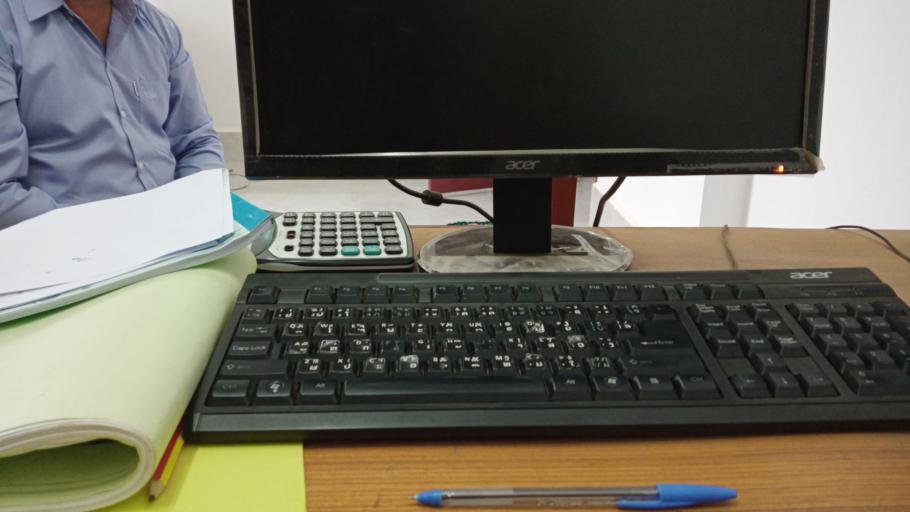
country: LA
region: Xiangkhoang
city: Phonsavan
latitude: 19.1079
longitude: 102.9254
